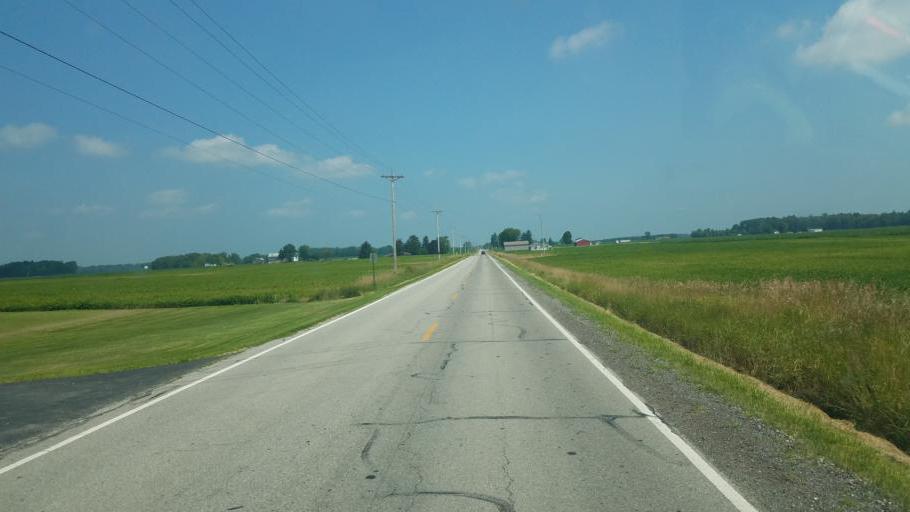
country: US
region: Ohio
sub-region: Huron County
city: Willard
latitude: 40.9711
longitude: -82.8535
